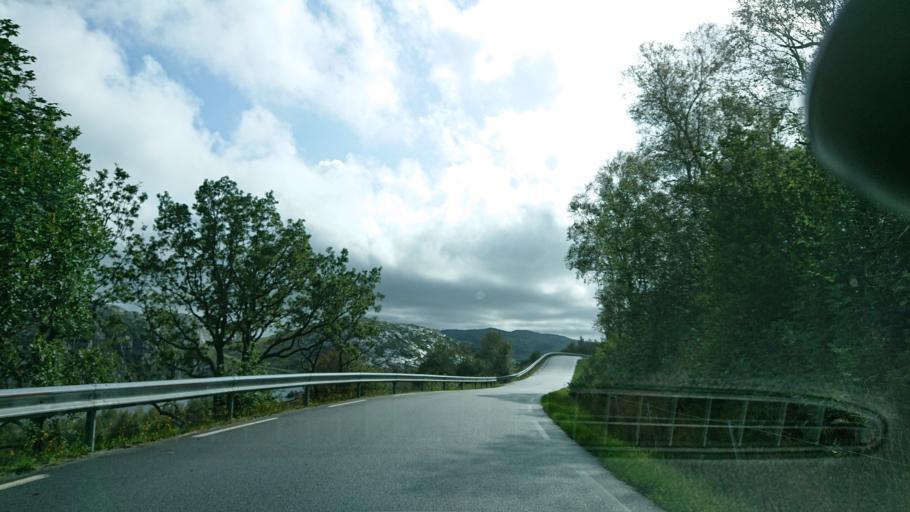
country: NO
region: Rogaland
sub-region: Gjesdal
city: Algard
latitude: 58.6920
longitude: 5.8804
